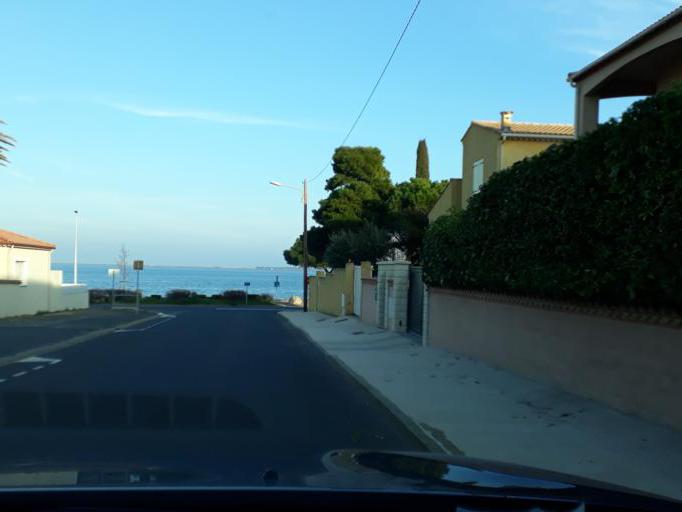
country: FR
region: Languedoc-Roussillon
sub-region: Departement de l'Herault
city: Marseillan
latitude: 43.3491
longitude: 3.5303
